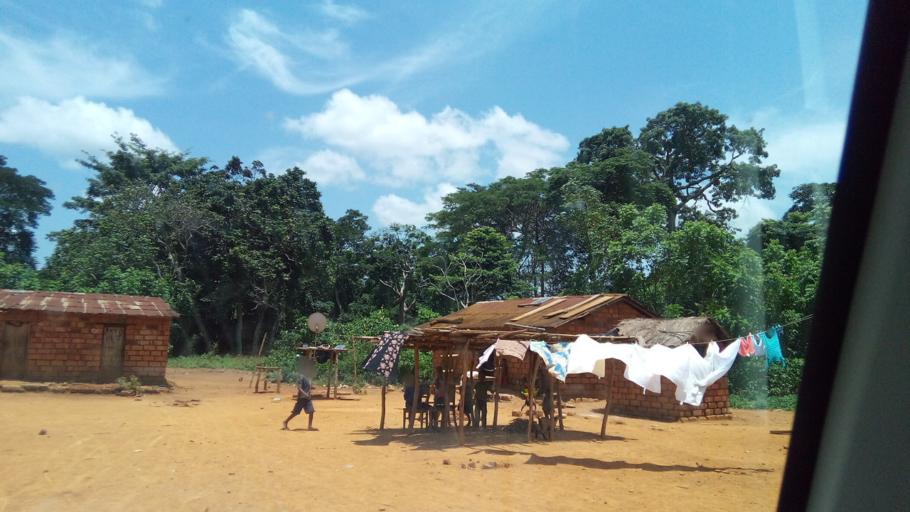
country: AO
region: Zaire
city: Mbanza Congo
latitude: -5.8024
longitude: 14.2450
